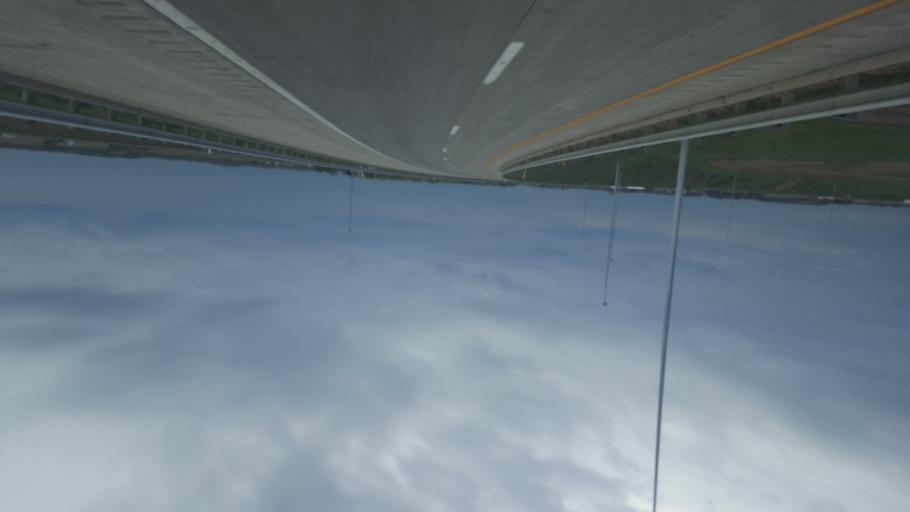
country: US
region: Ohio
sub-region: Wyandot County
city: Upper Sandusky
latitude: 40.8104
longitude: -83.2354
